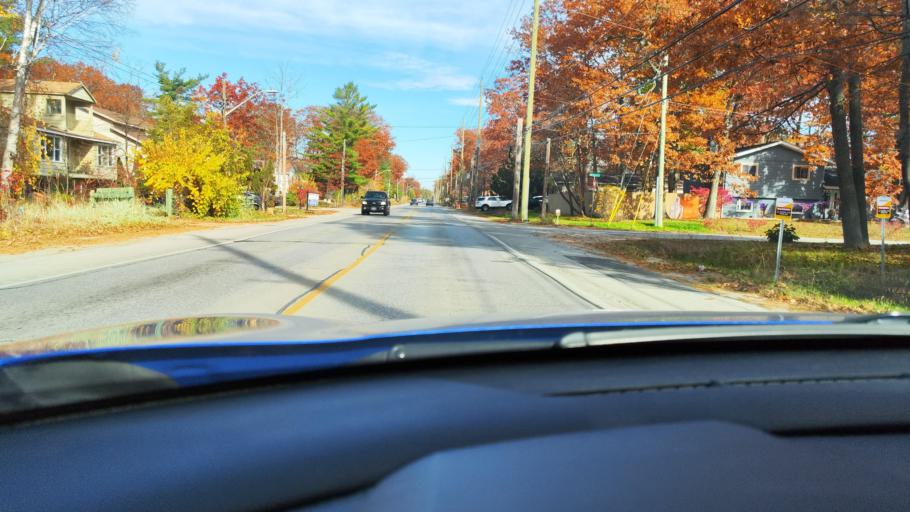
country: CA
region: Ontario
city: Wasaga Beach
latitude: 44.5038
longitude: -80.0335
